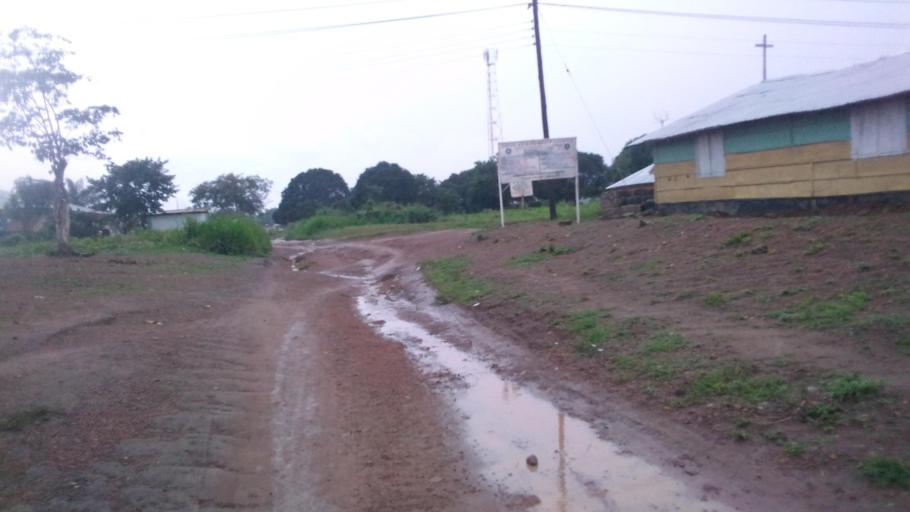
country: SL
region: Eastern Province
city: Kenema
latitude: 7.9023
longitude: -11.1669
